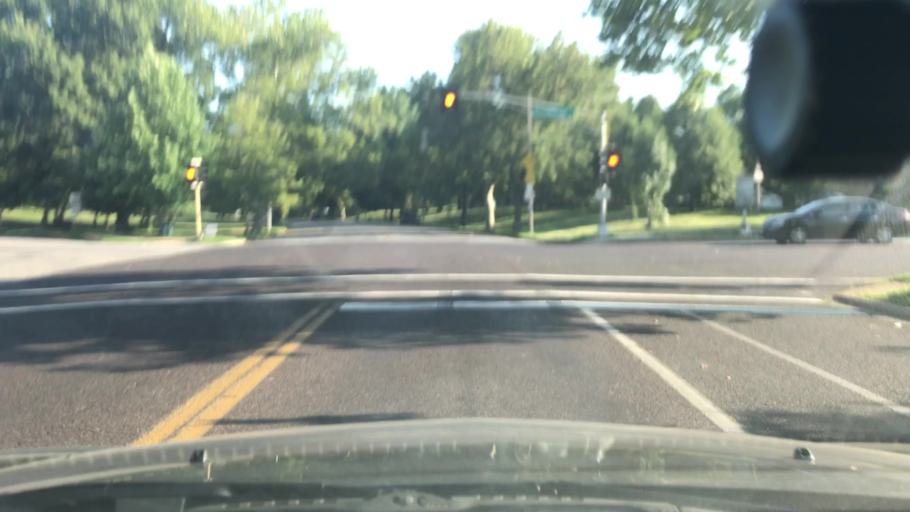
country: US
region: Missouri
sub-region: Saint Louis County
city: Lemay
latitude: 38.5795
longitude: -90.2757
